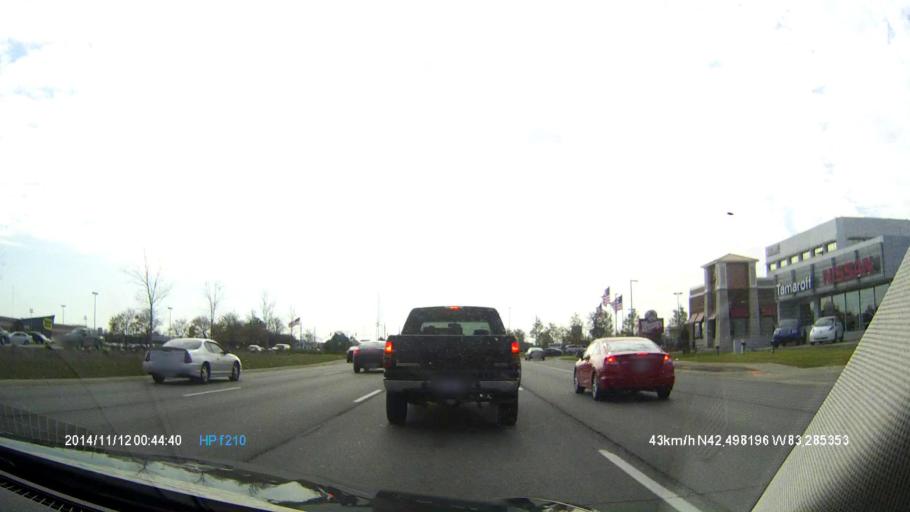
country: US
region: Michigan
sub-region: Oakland County
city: Bingham Farms
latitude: 42.4983
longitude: -83.2851
